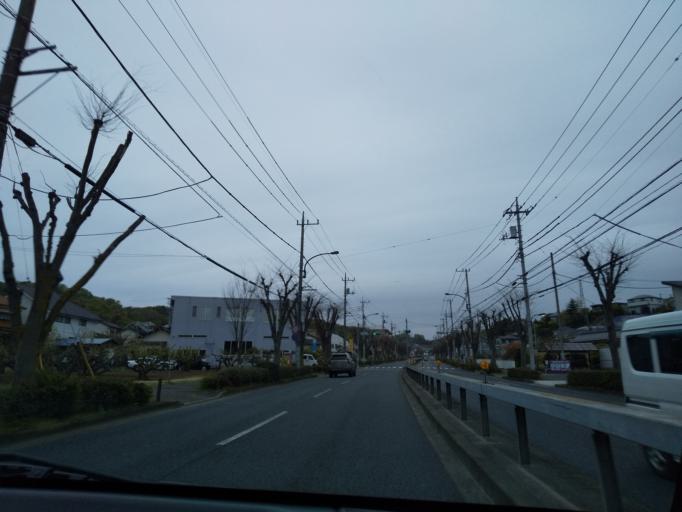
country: JP
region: Tokyo
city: Hino
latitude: 35.6301
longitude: 139.3773
